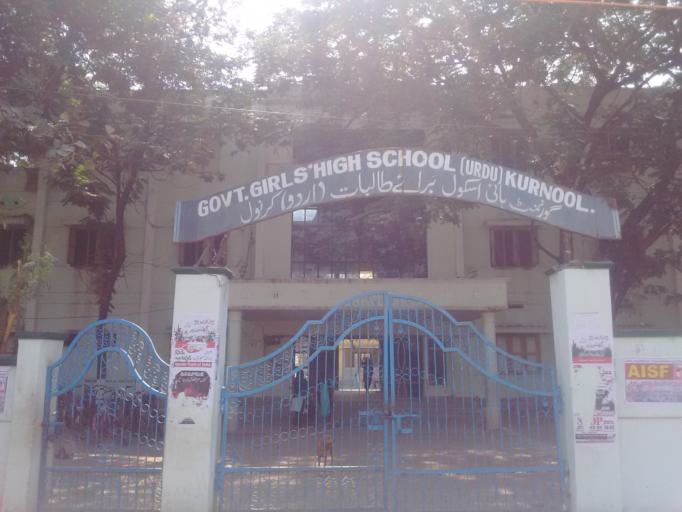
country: IN
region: Telangana
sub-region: Mahbubnagar
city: Alampur
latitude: 15.8323
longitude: 78.0436
